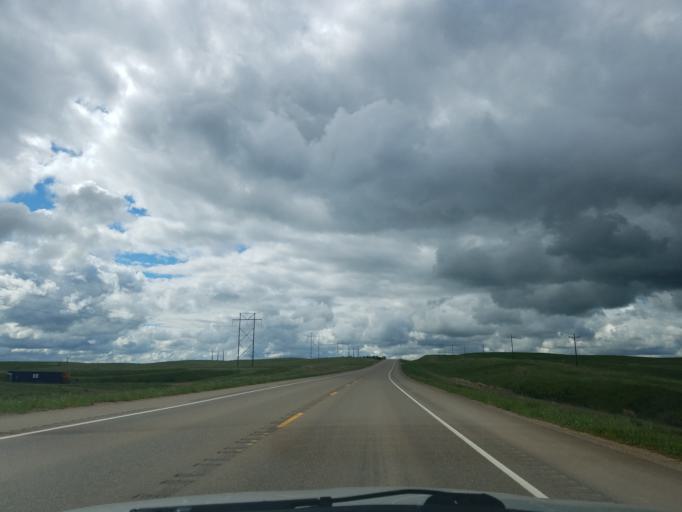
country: US
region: North Dakota
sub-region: McKenzie County
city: Watford City
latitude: 47.4660
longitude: -103.2473
